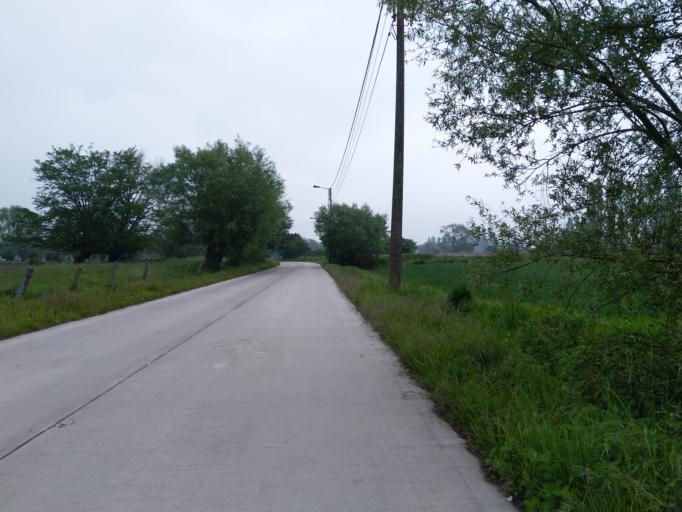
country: BE
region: Wallonia
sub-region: Province du Hainaut
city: Mons
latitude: 50.4636
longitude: 3.9102
